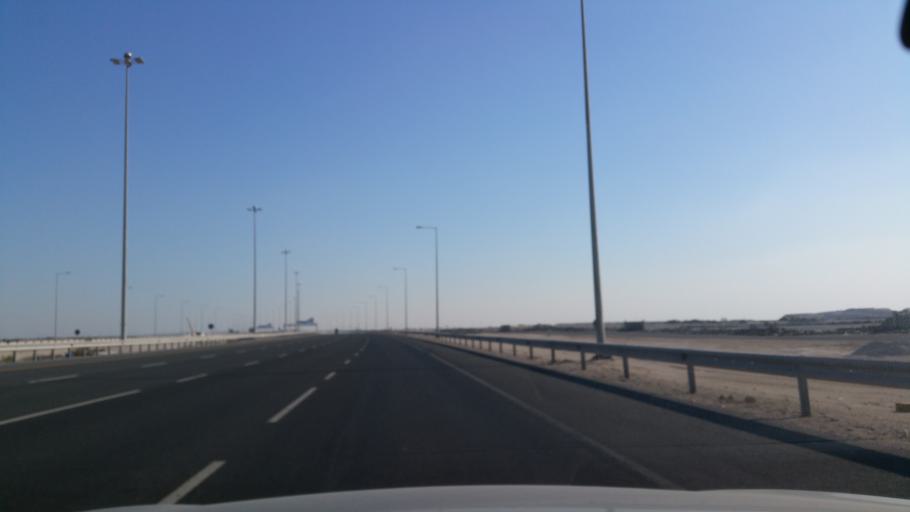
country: QA
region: Al Wakrah
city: Al Wukayr
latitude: 25.1473
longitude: 51.4745
